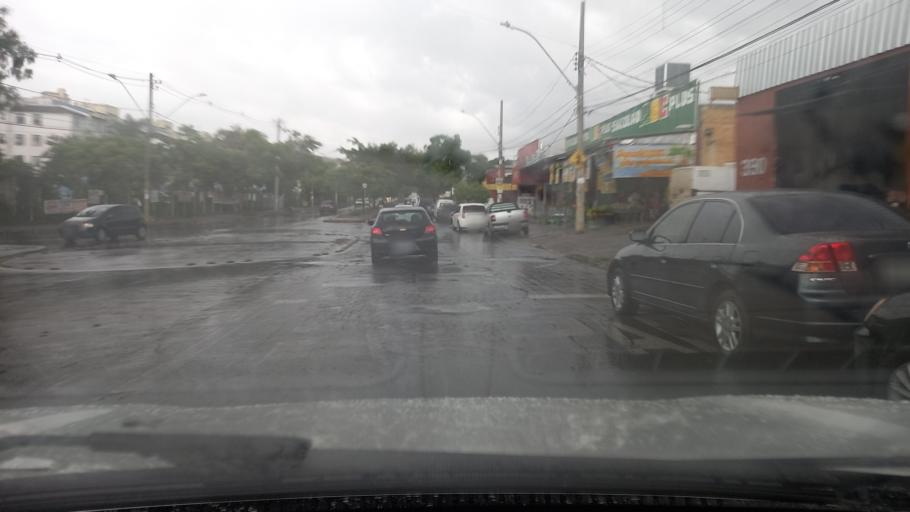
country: BR
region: Minas Gerais
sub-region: Contagem
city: Contagem
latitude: -19.8990
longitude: -44.0019
